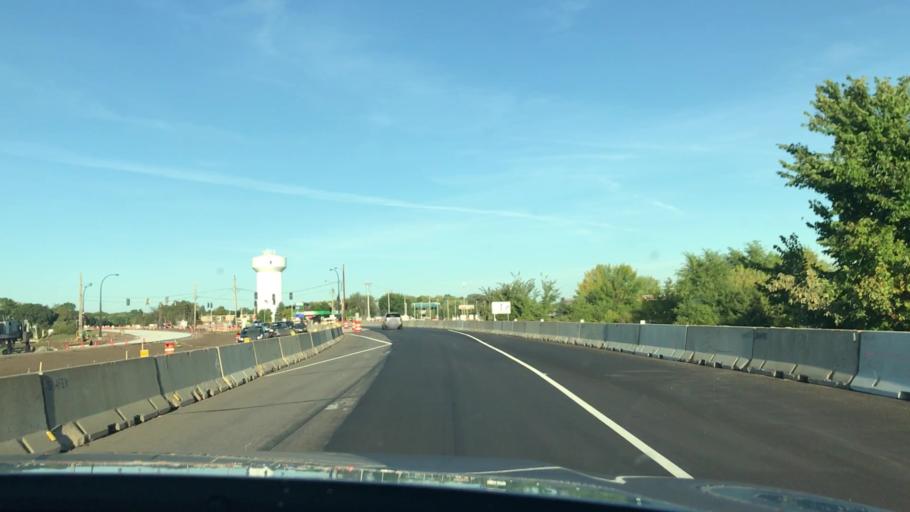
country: US
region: Minnesota
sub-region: Wright County
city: Otsego
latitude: 45.3060
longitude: -93.6115
